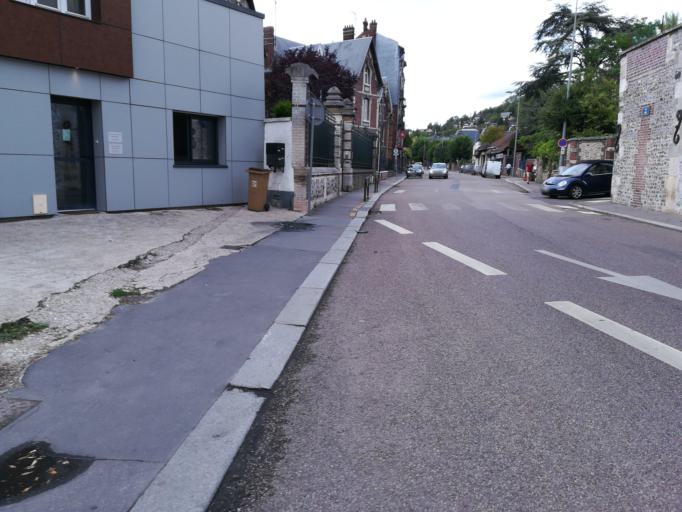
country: FR
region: Haute-Normandie
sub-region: Departement de la Seine-Maritime
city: Mont-Saint-Aignan
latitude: 49.4527
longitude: 1.0934
